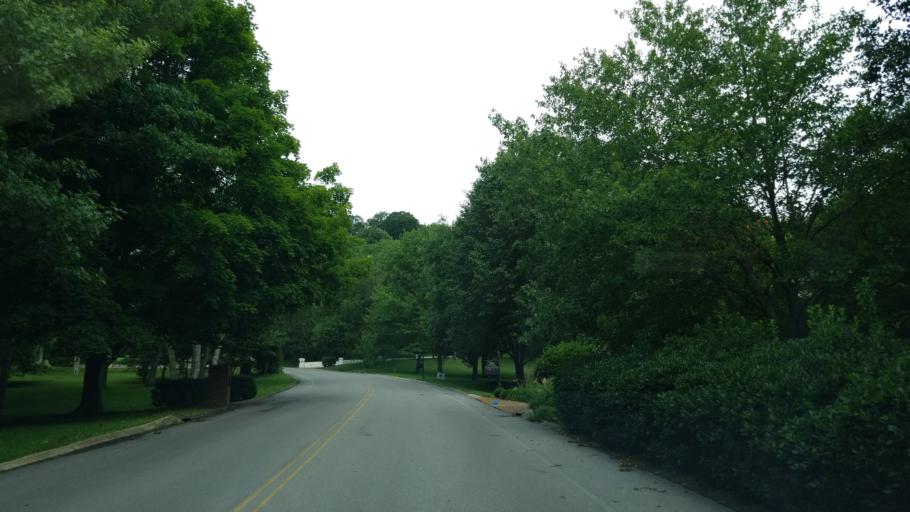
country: US
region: Tennessee
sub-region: Davidson County
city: Forest Hills
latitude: 36.0577
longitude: -86.8195
